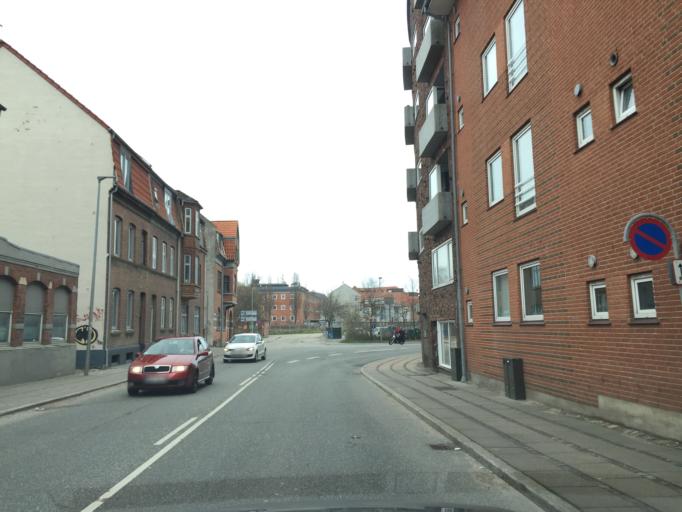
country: DK
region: South Denmark
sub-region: Kolding Kommune
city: Kolding
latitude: 55.4872
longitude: 9.4776
